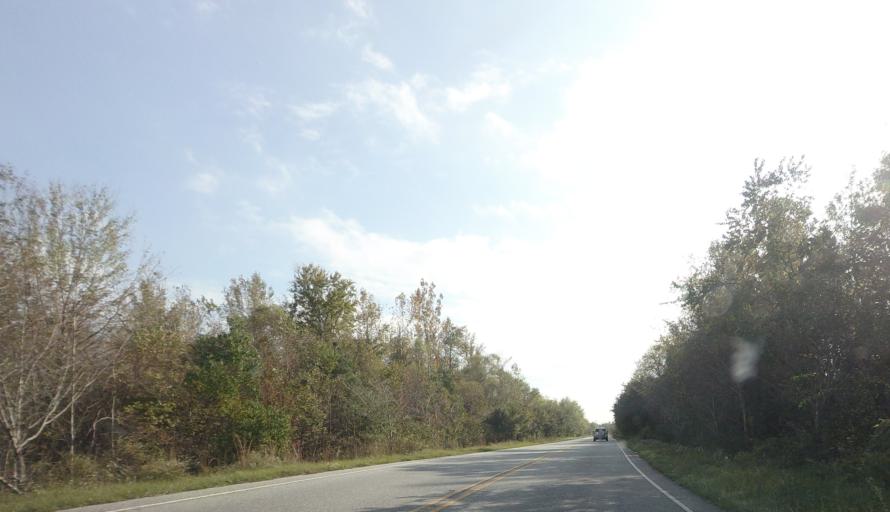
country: US
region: Georgia
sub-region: Bibb County
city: Macon
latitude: 32.8110
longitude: -83.6841
